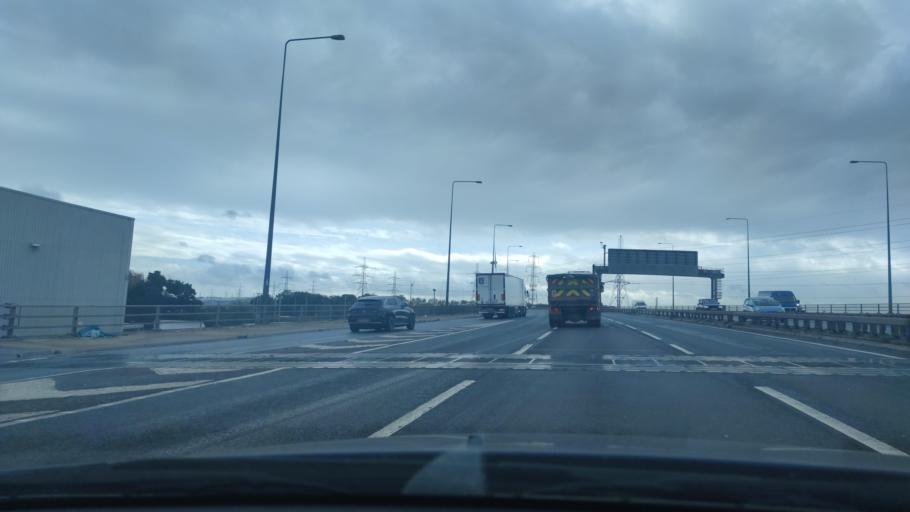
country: GB
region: England
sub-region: Greater London
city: Becontree
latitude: 51.5285
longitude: 0.1415
